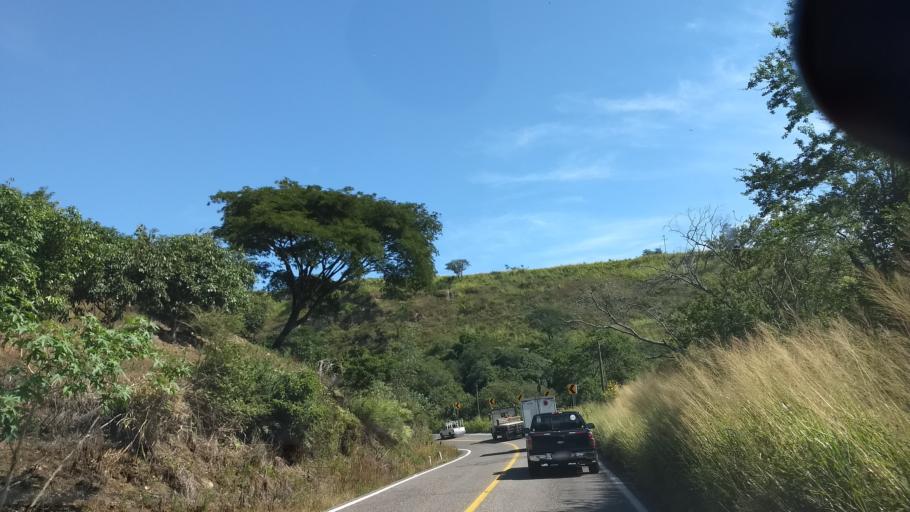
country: MX
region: Jalisco
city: Tuxpan
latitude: 19.5239
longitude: -103.4259
